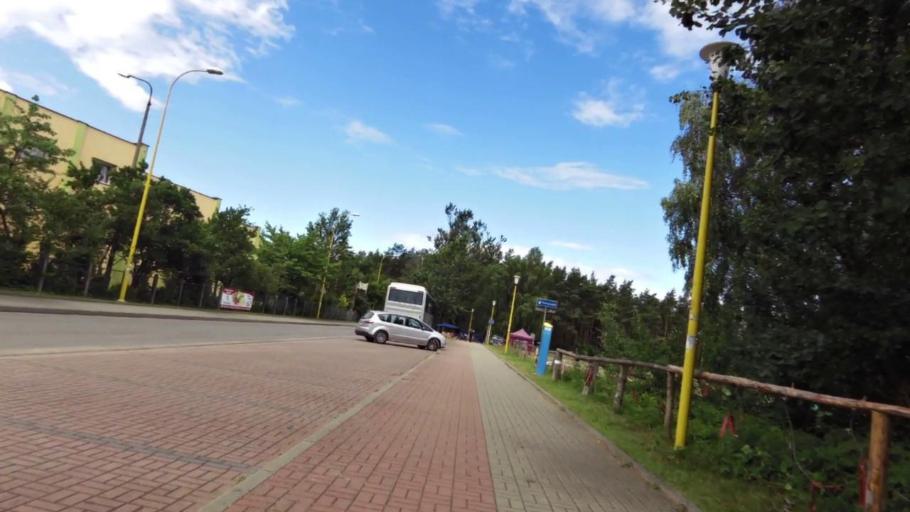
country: PL
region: West Pomeranian Voivodeship
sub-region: Powiat slawienski
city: Darlowo
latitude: 54.4446
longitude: 16.3954
